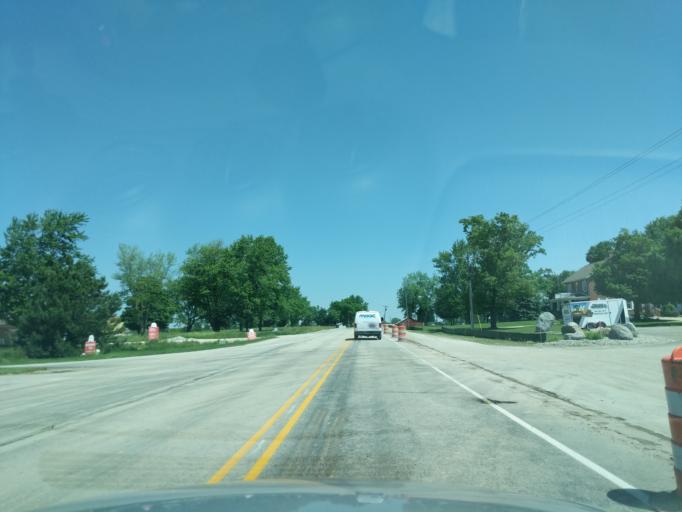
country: US
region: Indiana
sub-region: Whitley County
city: Columbia City
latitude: 41.1371
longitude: -85.4814
